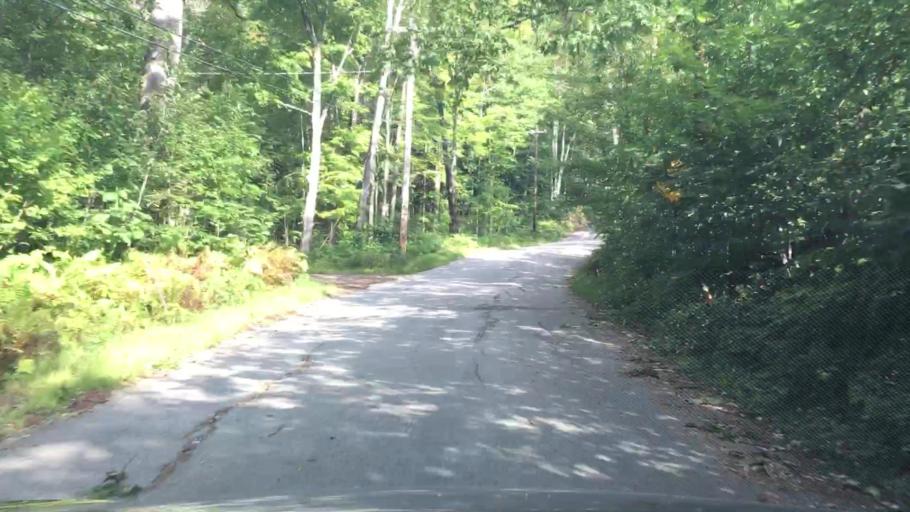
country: US
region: New Hampshire
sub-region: Grafton County
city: Littleton
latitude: 44.3125
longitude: -71.8812
